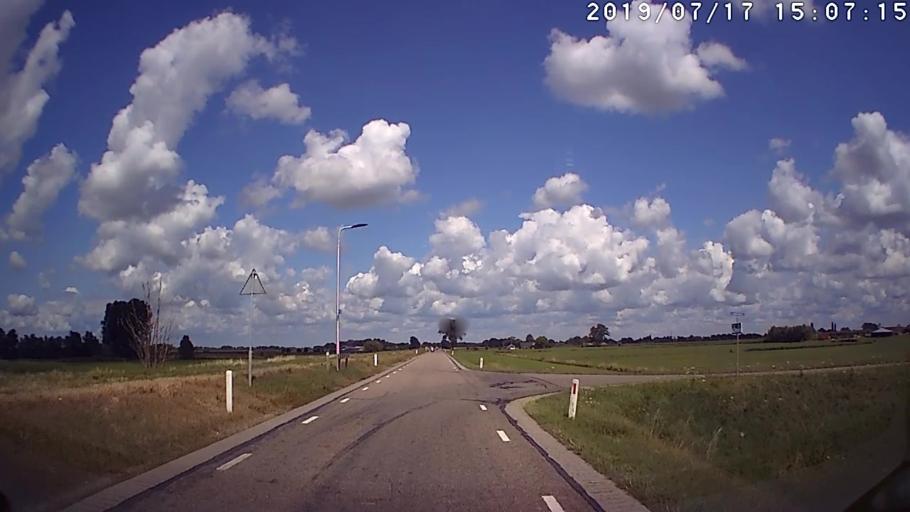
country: NL
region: Overijssel
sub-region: Gemeente Kampen
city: Kampen
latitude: 52.5180
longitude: 5.9860
